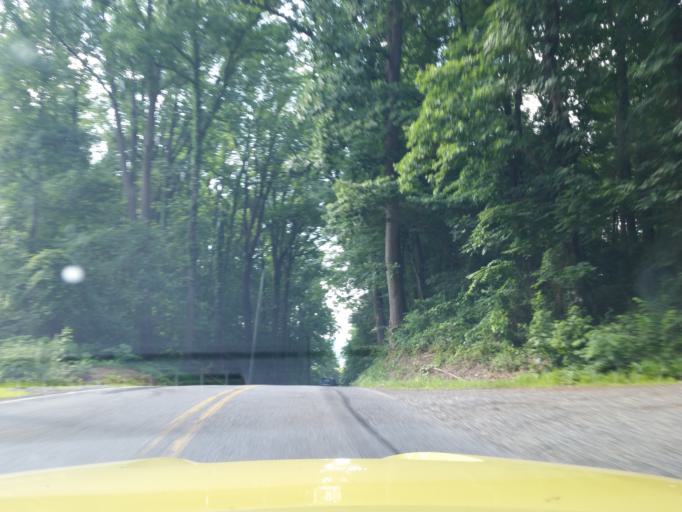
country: US
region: Pennsylvania
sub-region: Lebanon County
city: Campbelltown
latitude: 40.2350
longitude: -76.5086
